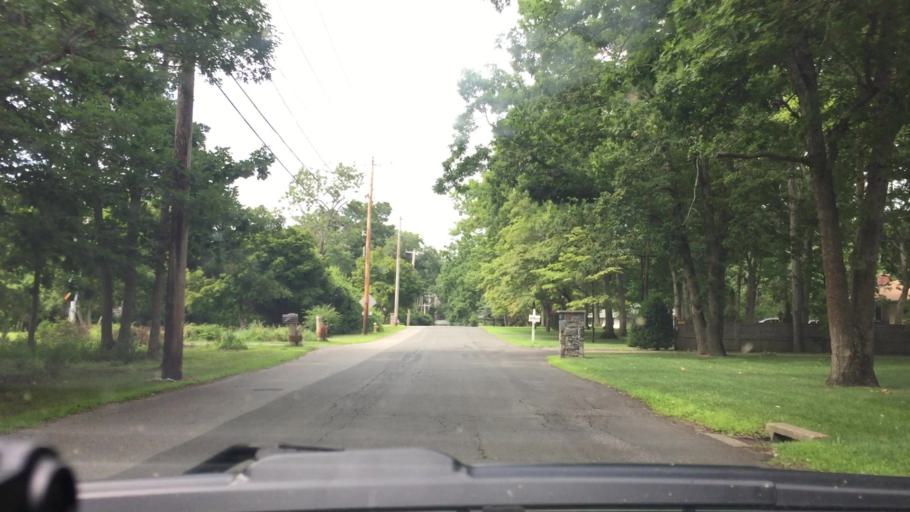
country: US
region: New York
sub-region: Suffolk County
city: Mount Sinai
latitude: 40.9224
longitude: -73.0145
